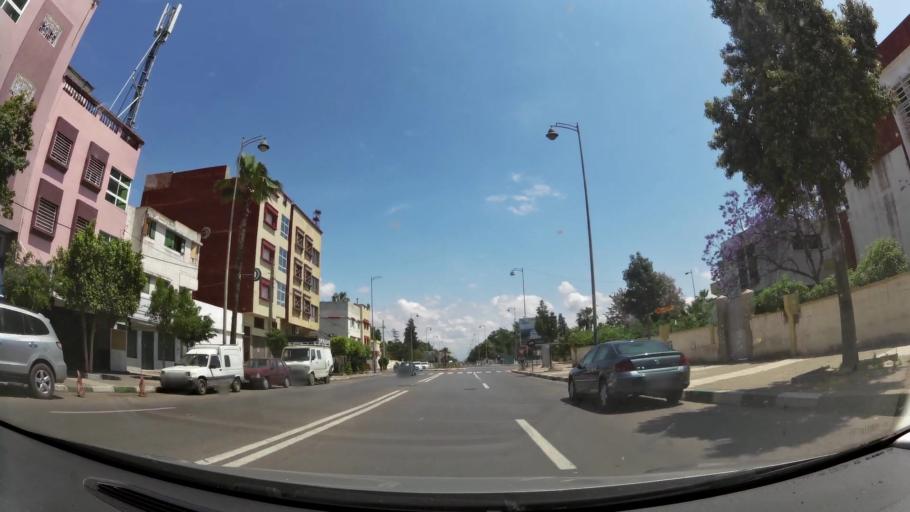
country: MA
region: Gharb-Chrarda-Beni Hssen
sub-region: Kenitra Province
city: Kenitra
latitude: 34.2539
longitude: -6.5594
